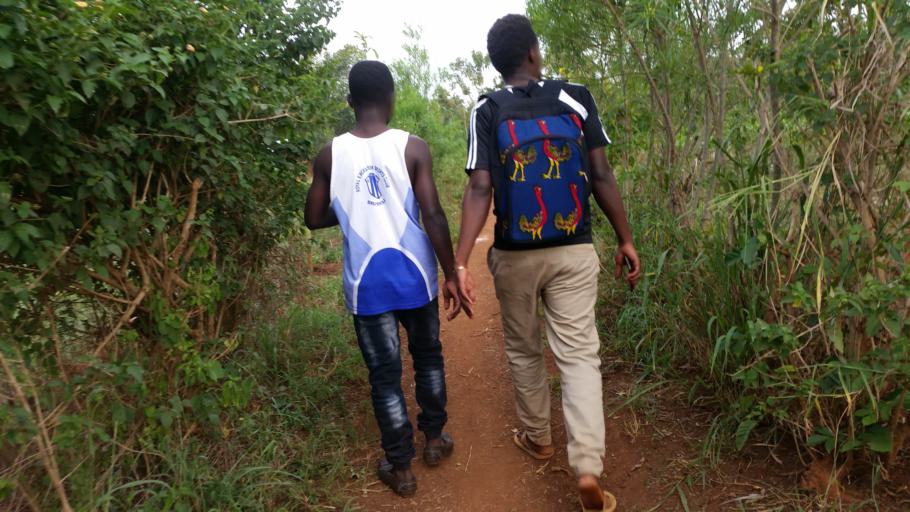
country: UG
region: Eastern Region
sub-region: Busia District
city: Busia
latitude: 0.5363
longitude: 34.0344
